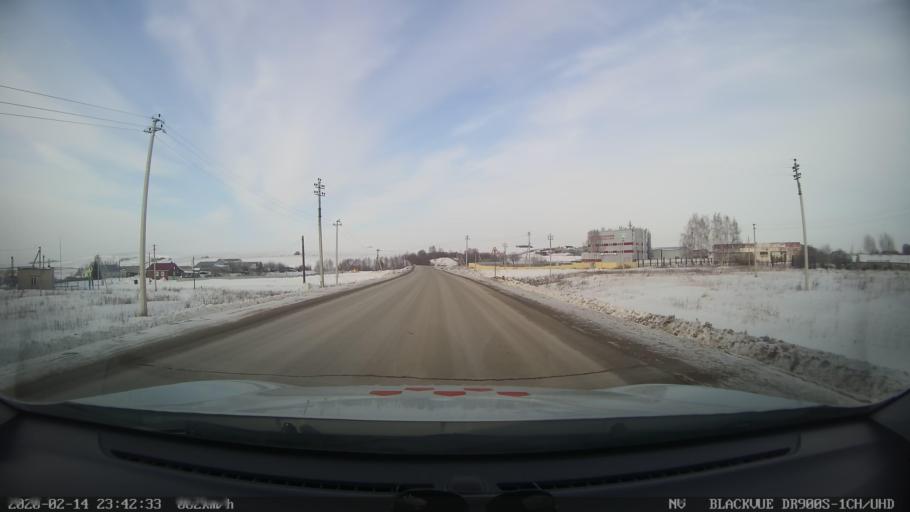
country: RU
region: Tatarstan
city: Kuybyshevskiy Zaton
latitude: 55.1926
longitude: 49.2472
